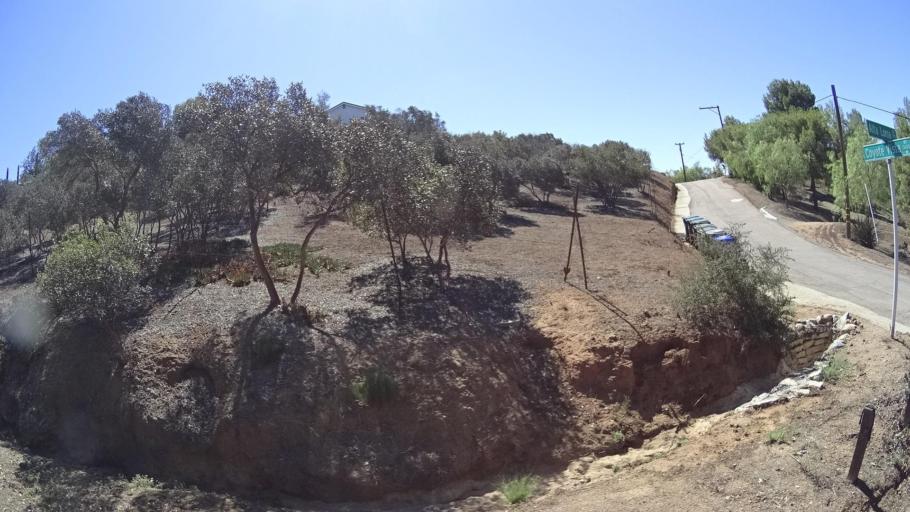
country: US
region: California
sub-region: San Diego County
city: Jamul
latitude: 32.7393
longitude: -116.8737
